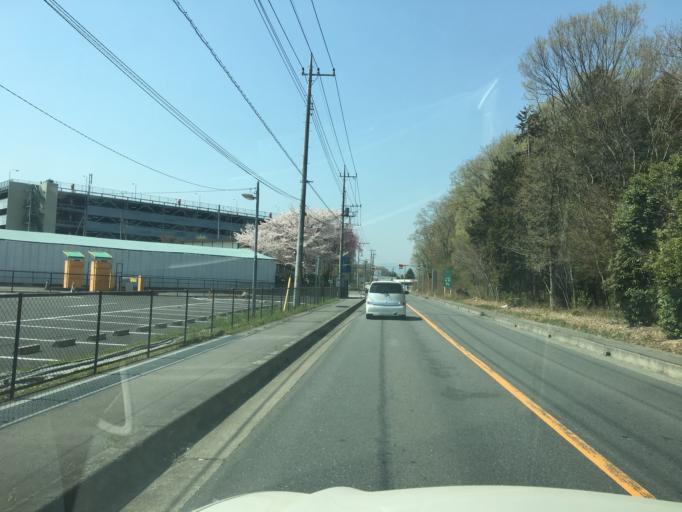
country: JP
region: Saitama
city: Sayama
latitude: 35.8119
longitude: 139.3824
